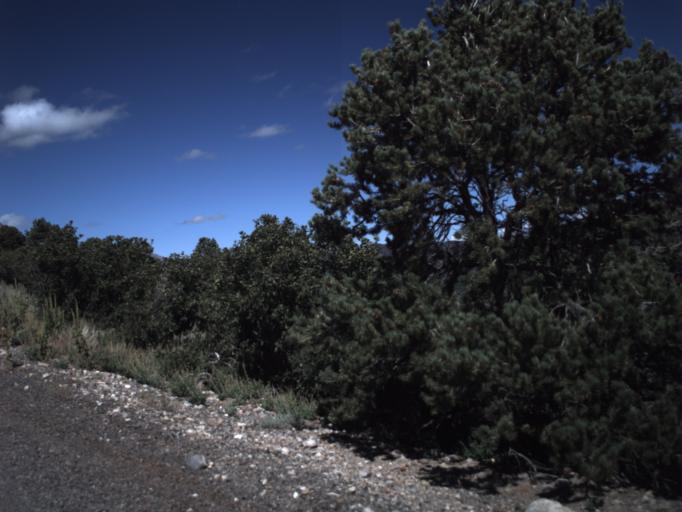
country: US
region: Utah
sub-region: Piute County
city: Junction
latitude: 38.2510
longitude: -112.3131
